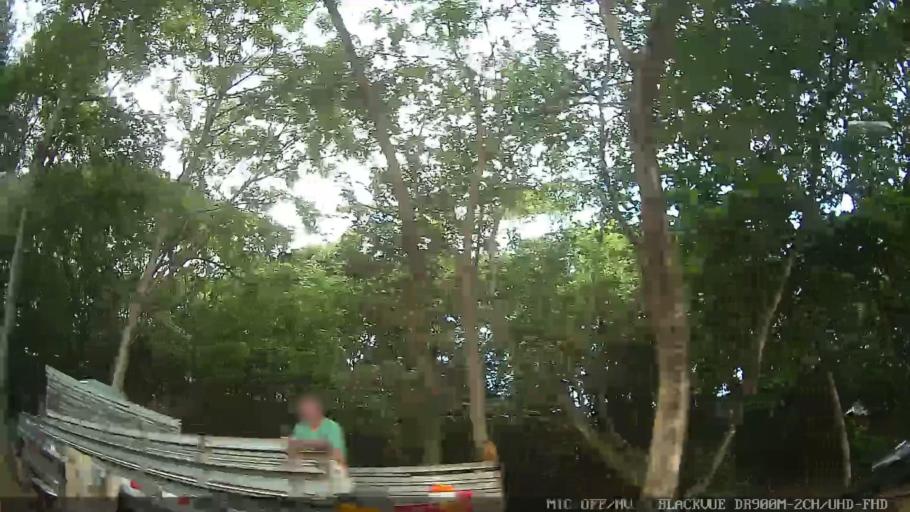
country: BR
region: Sao Paulo
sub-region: Pedreira
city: Pedreira
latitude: -22.7189
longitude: -46.8922
